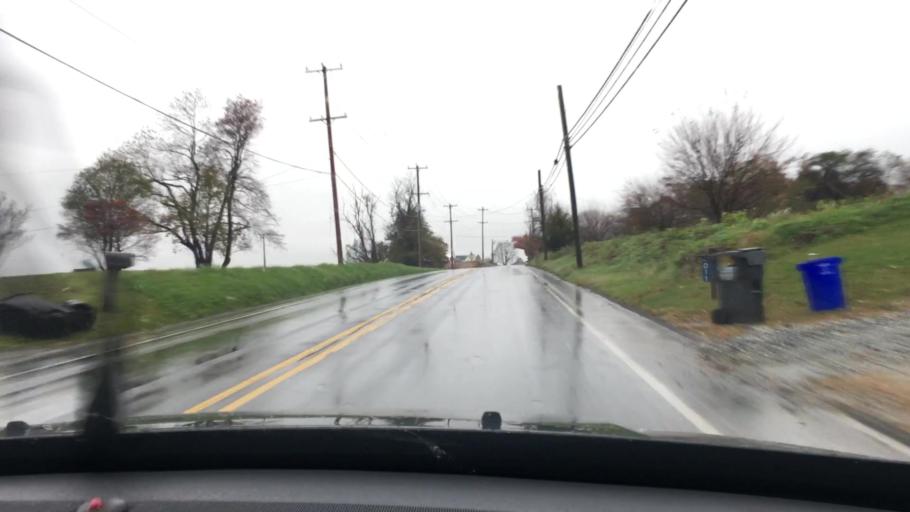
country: US
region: Pennsylvania
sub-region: York County
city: Susquehanna Trails
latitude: 39.8145
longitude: -76.3813
